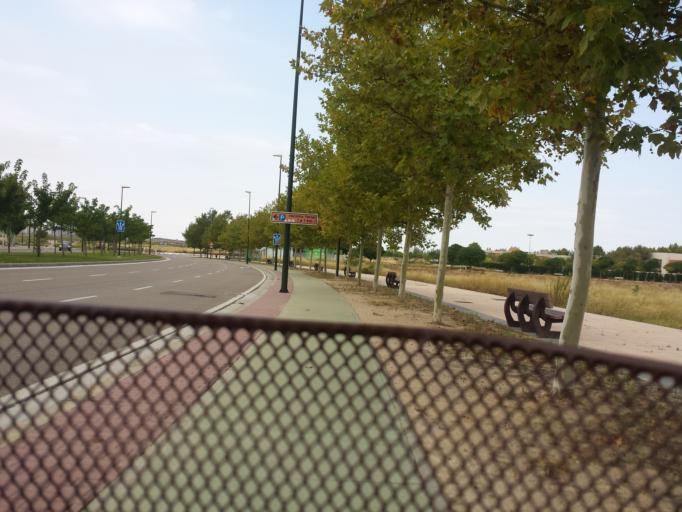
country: ES
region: Aragon
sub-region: Provincia de Zaragoza
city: Montecanal
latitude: 41.6241
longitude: -0.9398
